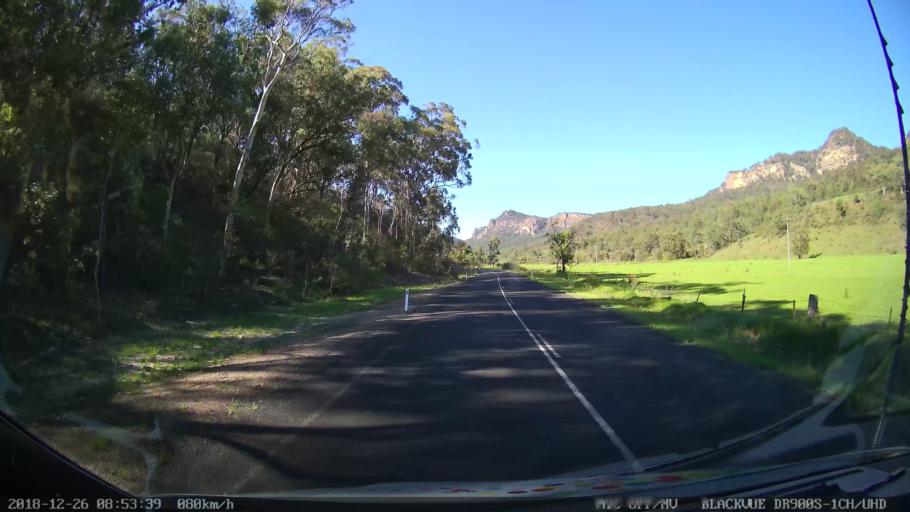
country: AU
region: New South Wales
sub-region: Mid-Western Regional
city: Kandos
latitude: -32.6065
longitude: 150.0765
